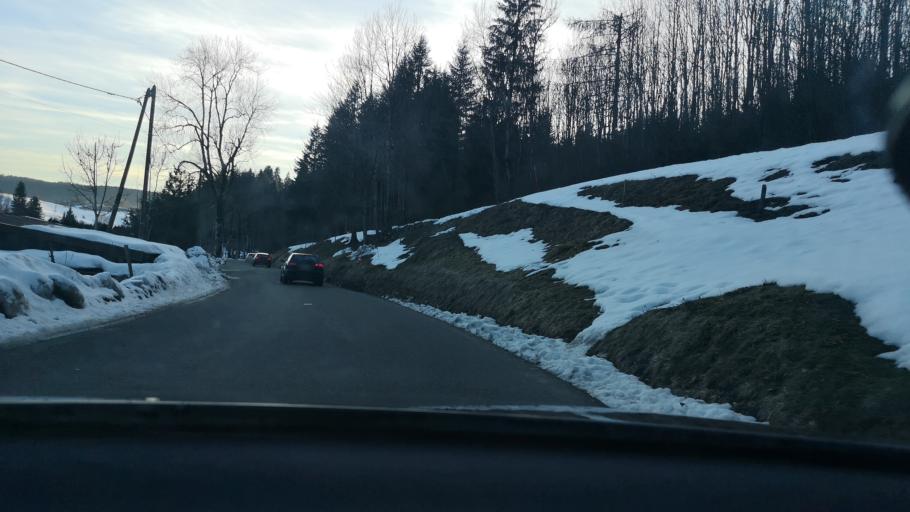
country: FR
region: Franche-Comte
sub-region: Departement du Doubs
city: Pontarlier
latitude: 46.9120
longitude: 6.3803
